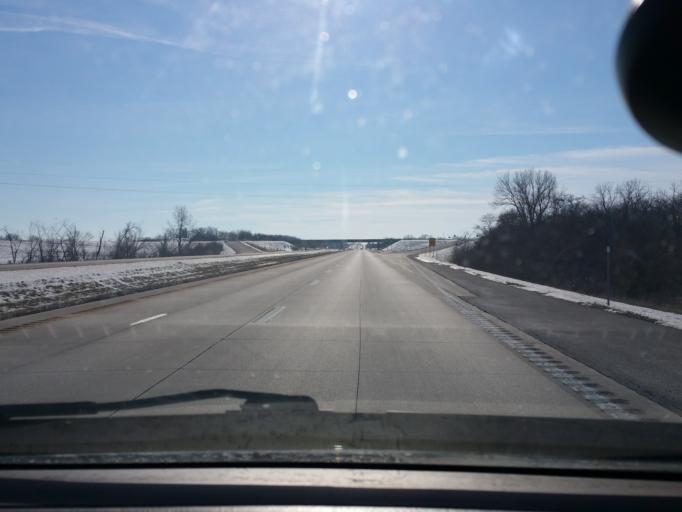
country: US
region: Missouri
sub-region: Daviess County
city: Gallatin
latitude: 40.0009
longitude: -94.0962
